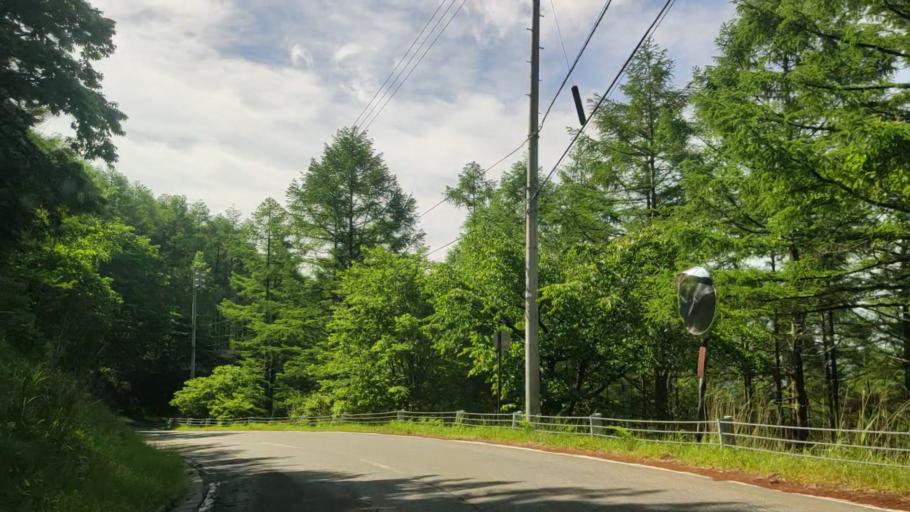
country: JP
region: Nagano
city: Suwa
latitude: 36.0979
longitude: 138.1421
